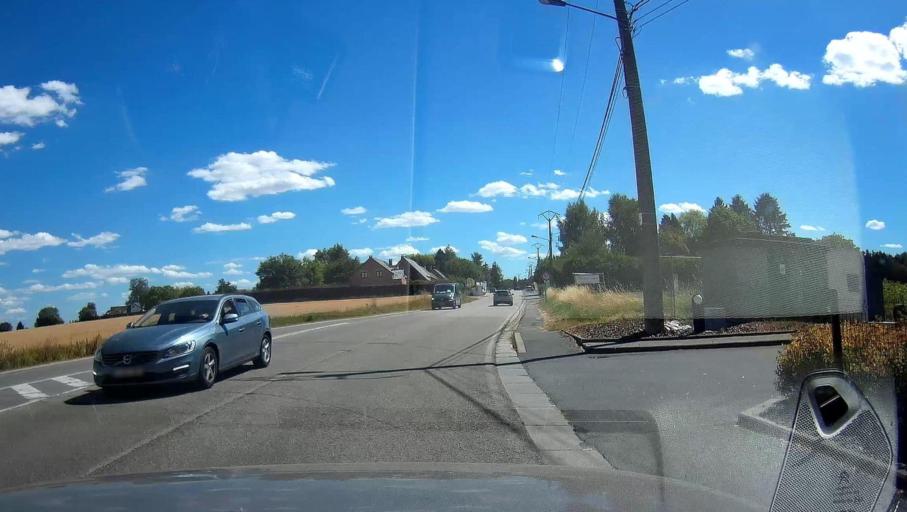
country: BE
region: Wallonia
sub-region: Province du Hainaut
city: Gerpinnes
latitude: 50.3459
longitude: 4.4854
